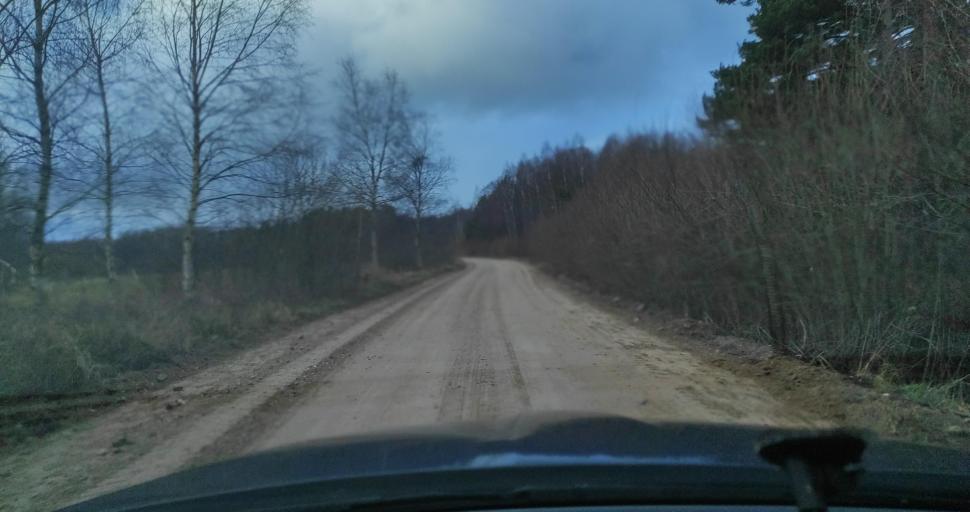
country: LV
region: Pavilostas
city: Pavilosta
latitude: 56.8555
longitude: 21.1317
